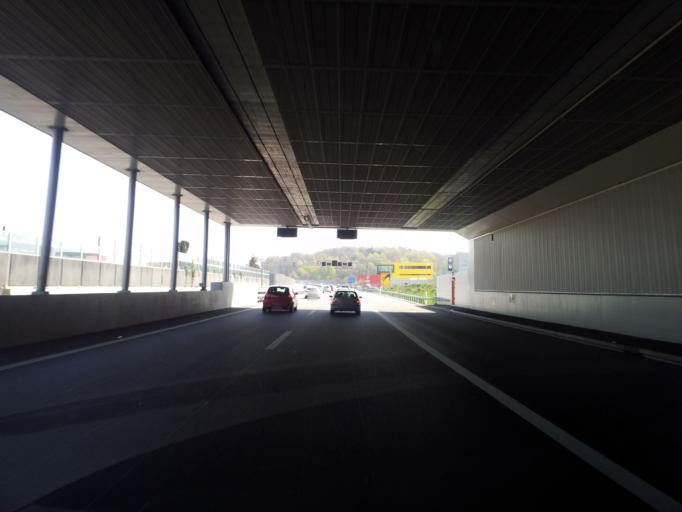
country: CH
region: Aargau
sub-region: Bezirk Lenzburg
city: Niederlenz
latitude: 47.3954
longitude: 8.1714
